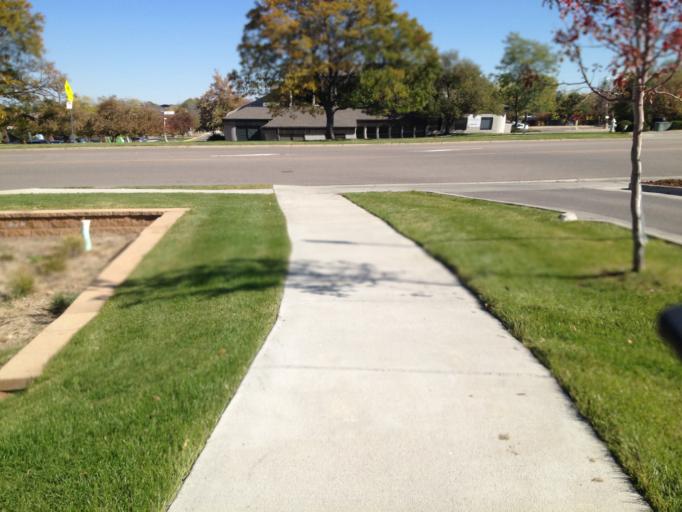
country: US
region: Colorado
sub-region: Boulder County
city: Boulder
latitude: 39.9851
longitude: -105.2398
